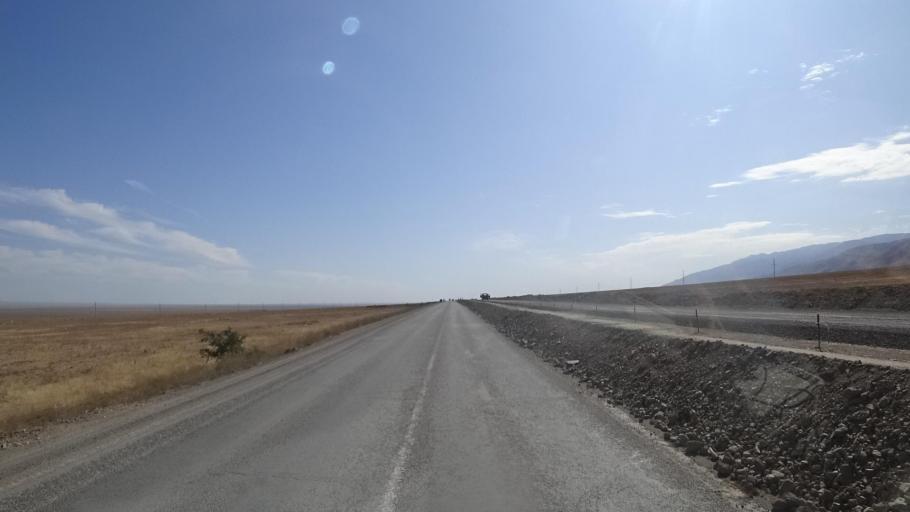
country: KG
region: Chuy
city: Ivanovka
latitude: 43.3841
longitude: 75.1768
